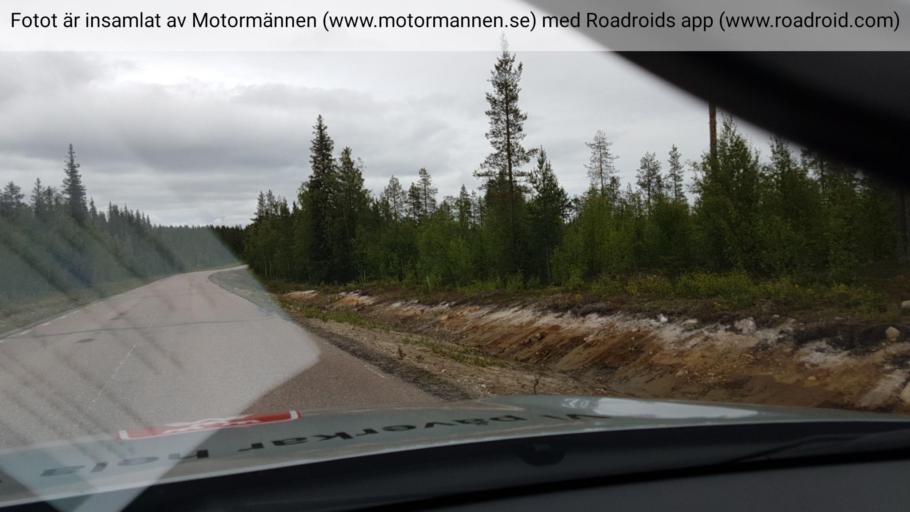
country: SE
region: Norrbotten
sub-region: Overkalix Kommun
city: OEverkalix
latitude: 67.0617
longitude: 22.2355
